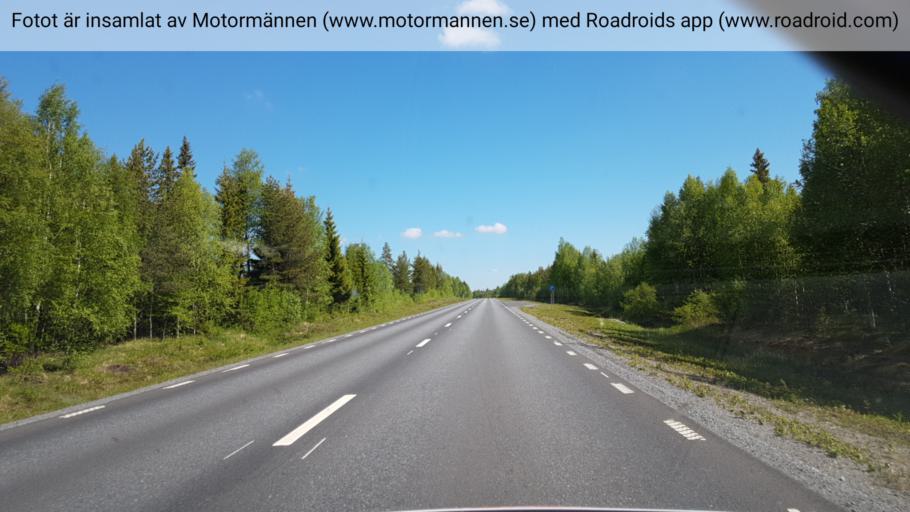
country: SE
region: Vaesterbotten
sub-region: Dorotea Kommun
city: Dorotea
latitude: 64.3291
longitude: 16.6306
